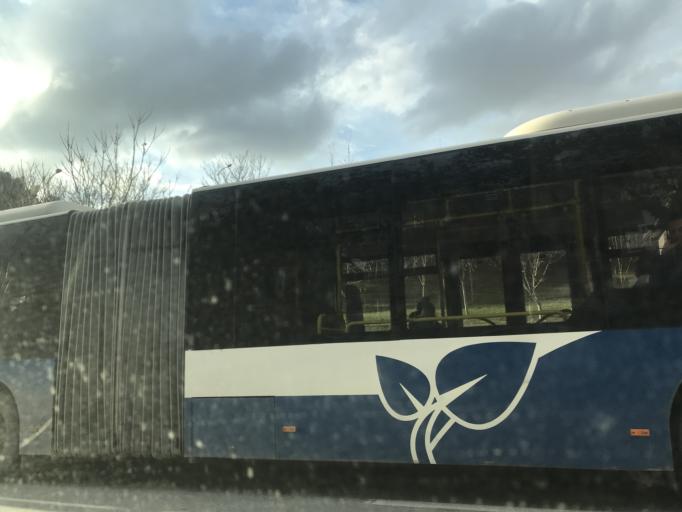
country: TR
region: Ankara
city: Mamak
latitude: 39.9652
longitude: 32.8723
